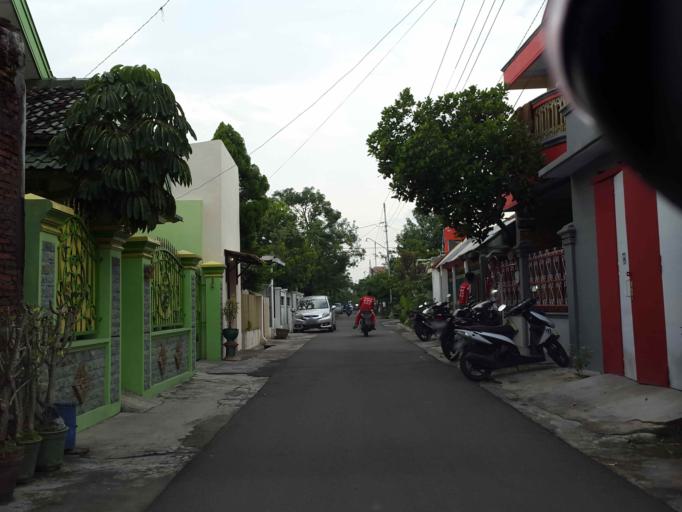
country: ID
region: Central Java
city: Surakarta
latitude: -7.5506
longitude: 110.8069
